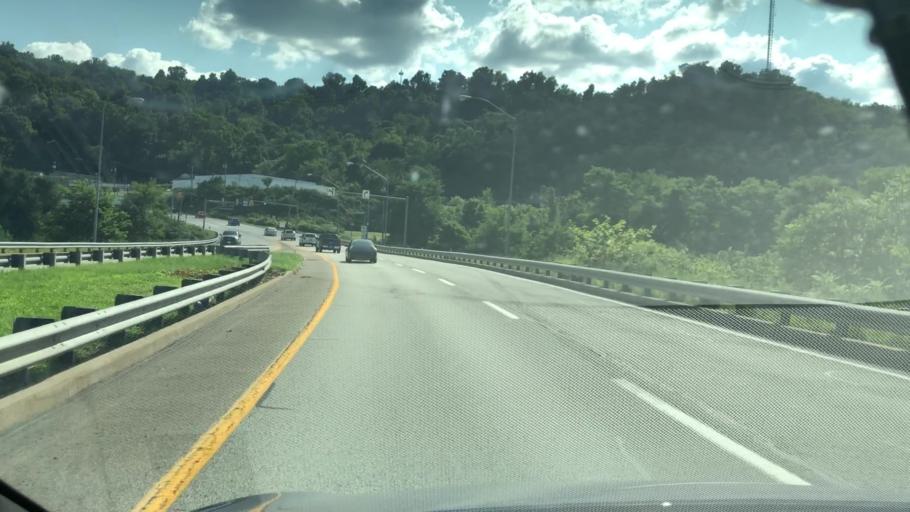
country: US
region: Pennsylvania
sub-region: Allegheny County
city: Pitcairn
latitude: 40.3947
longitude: -79.7743
